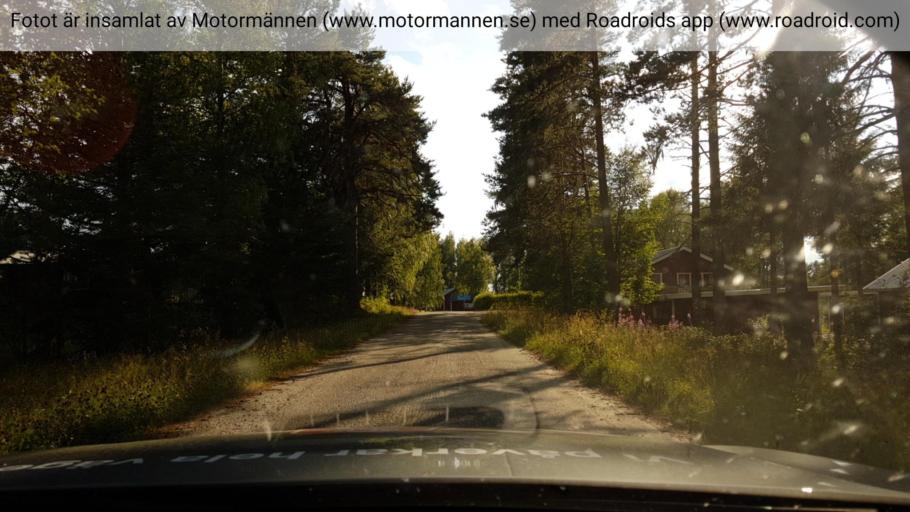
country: SE
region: Jaemtland
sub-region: Stroemsunds Kommun
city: Stroemsund
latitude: 63.7165
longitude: 15.8609
